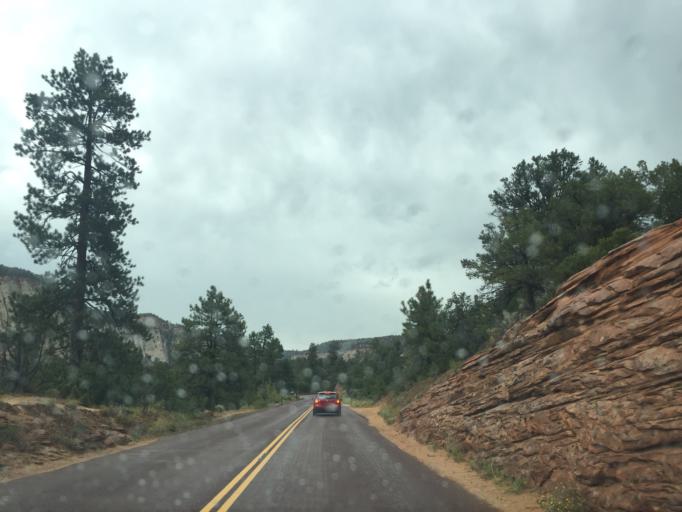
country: US
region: Utah
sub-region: Washington County
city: Hildale
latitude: 37.2287
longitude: -112.8789
